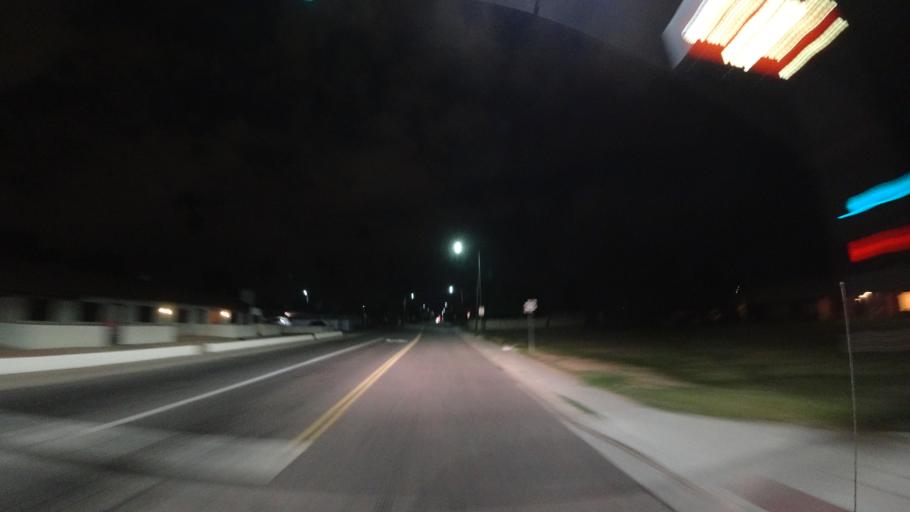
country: US
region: Arizona
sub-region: Maricopa County
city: Chandler
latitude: 33.3206
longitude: -111.8505
